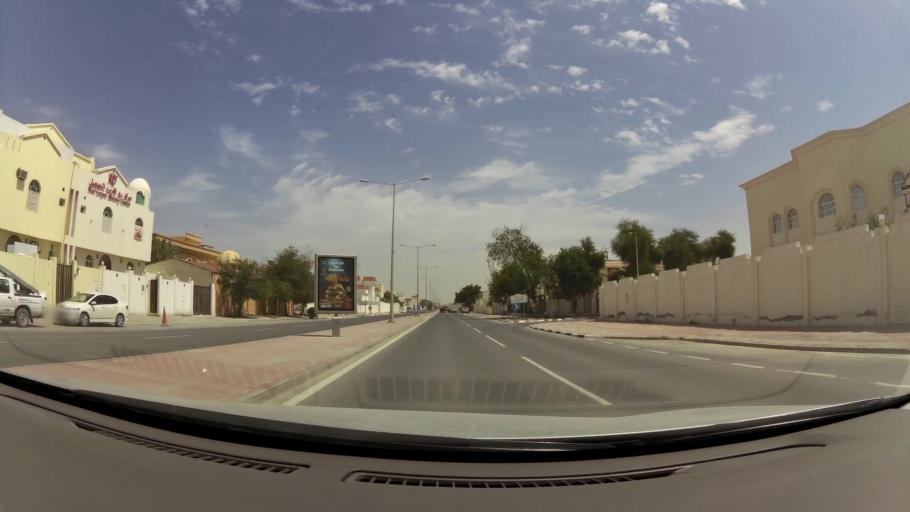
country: QA
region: Baladiyat ar Rayyan
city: Ar Rayyan
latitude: 25.2838
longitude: 51.4123
